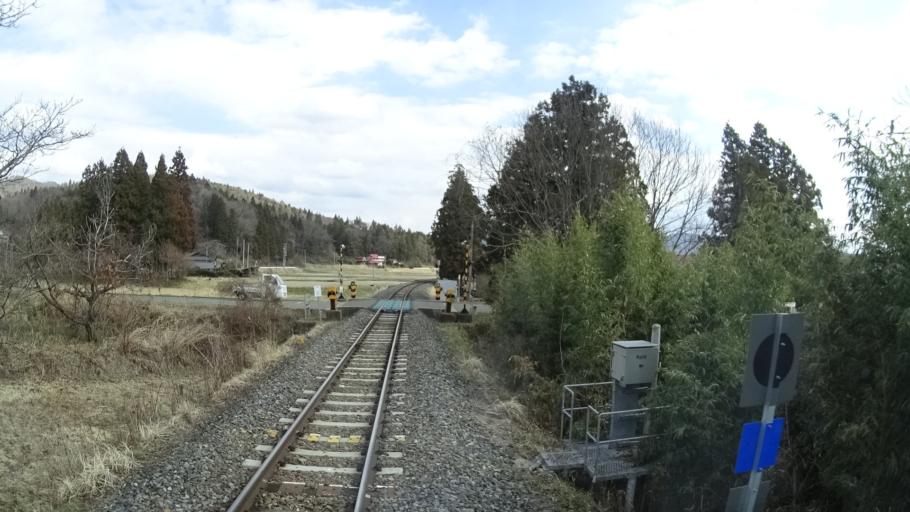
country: JP
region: Iwate
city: Hanamaki
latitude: 39.3755
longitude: 141.2519
